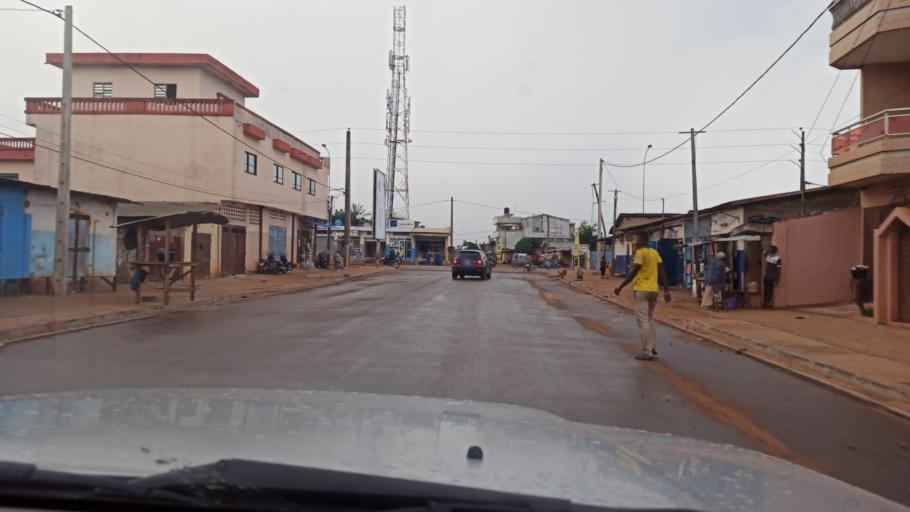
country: BJ
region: Queme
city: Porto-Novo
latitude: 6.4965
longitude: 2.6399
